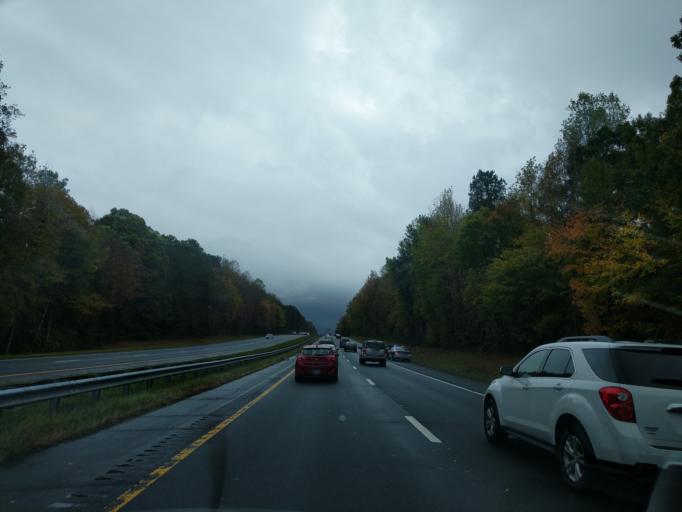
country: US
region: North Carolina
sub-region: Orange County
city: Hillsborough
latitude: 36.0537
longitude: -79.0669
